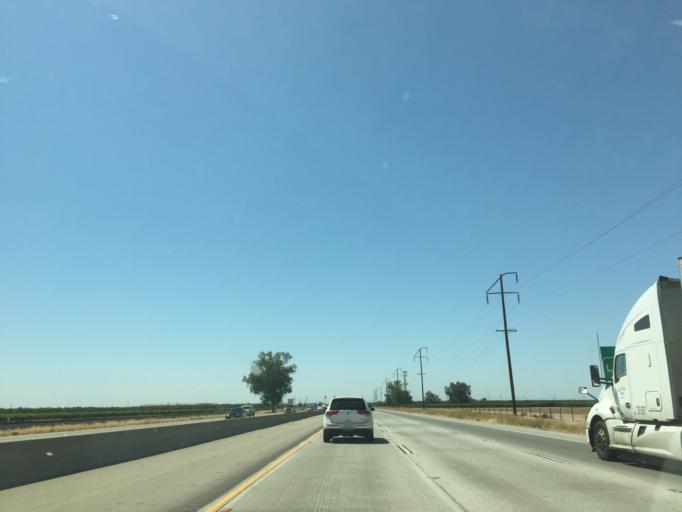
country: US
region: California
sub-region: Kern County
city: Rosedale
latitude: 35.4862
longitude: -119.1464
